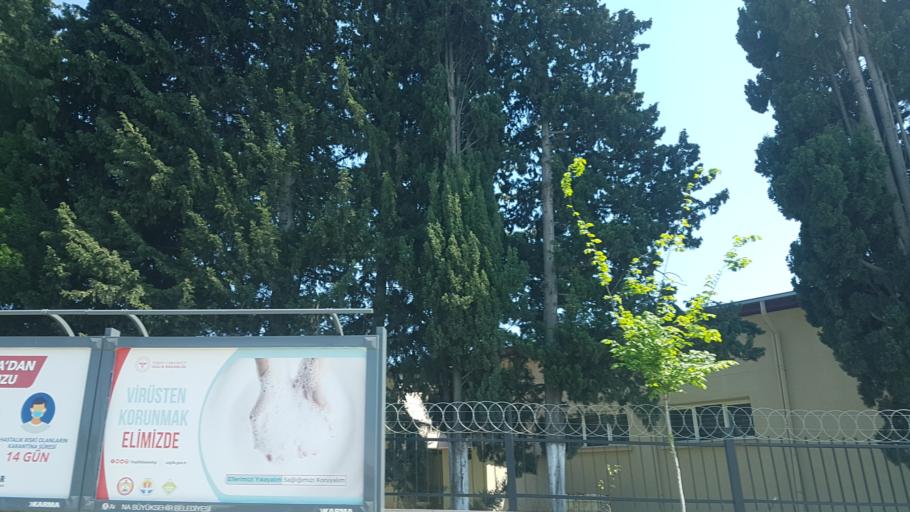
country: TR
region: Adana
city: Adana
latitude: 37.0134
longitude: 35.3378
